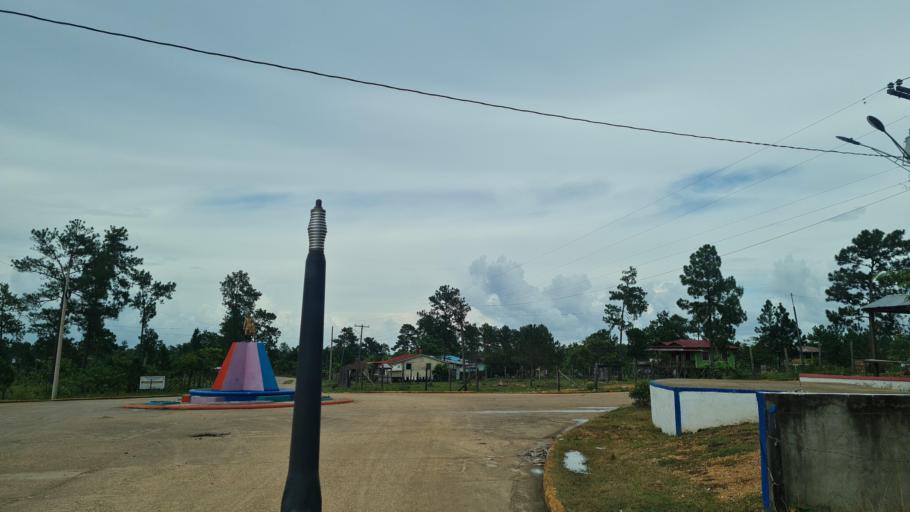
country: NI
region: Atlantico Norte (RAAN)
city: Waspam
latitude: 14.7212
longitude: -83.9771
